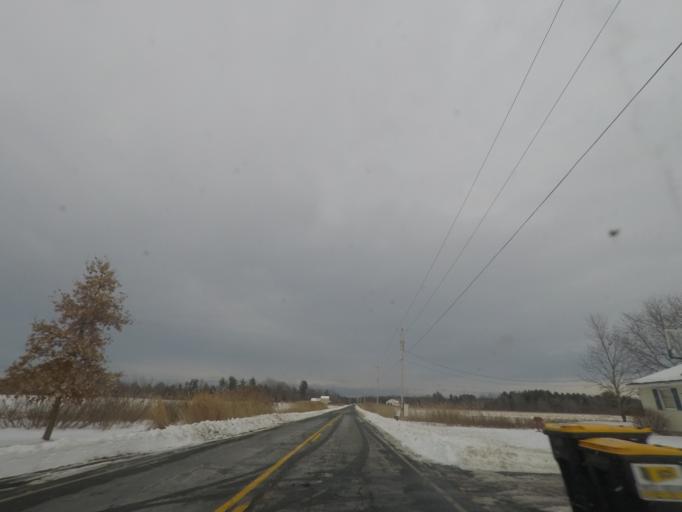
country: US
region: New York
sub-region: Rensselaer County
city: Castleton-on-Hudson
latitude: 42.5170
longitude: -73.7433
